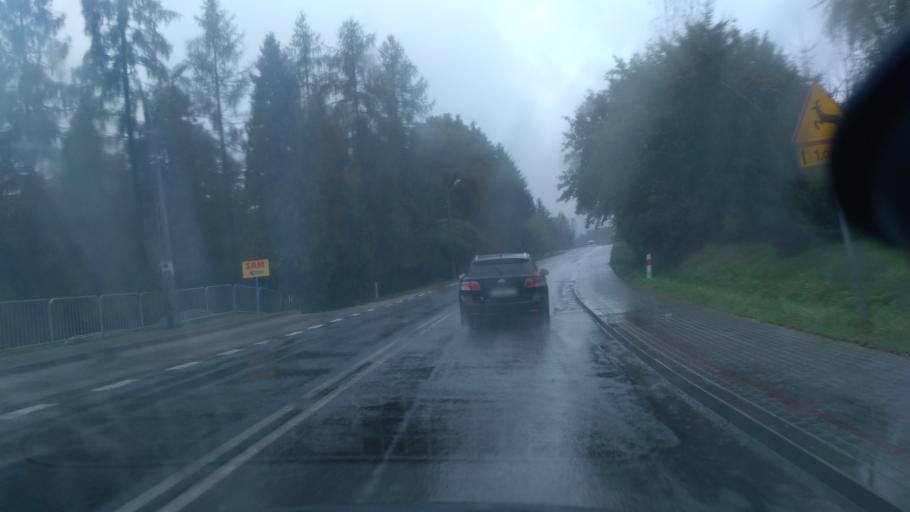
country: PL
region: Subcarpathian Voivodeship
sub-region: Powiat ropczycko-sedziszowski
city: Niedzwiada
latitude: 49.9988
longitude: 21.5616
